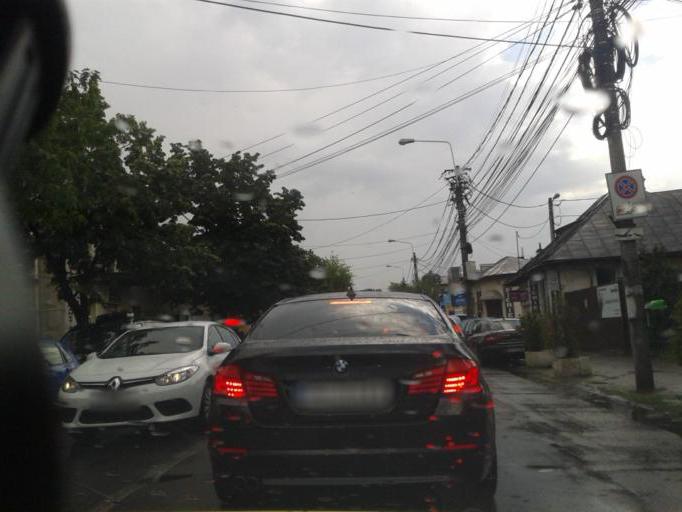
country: RO
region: Prahova
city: Ploiesti
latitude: 44.9453
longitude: 26.0241
